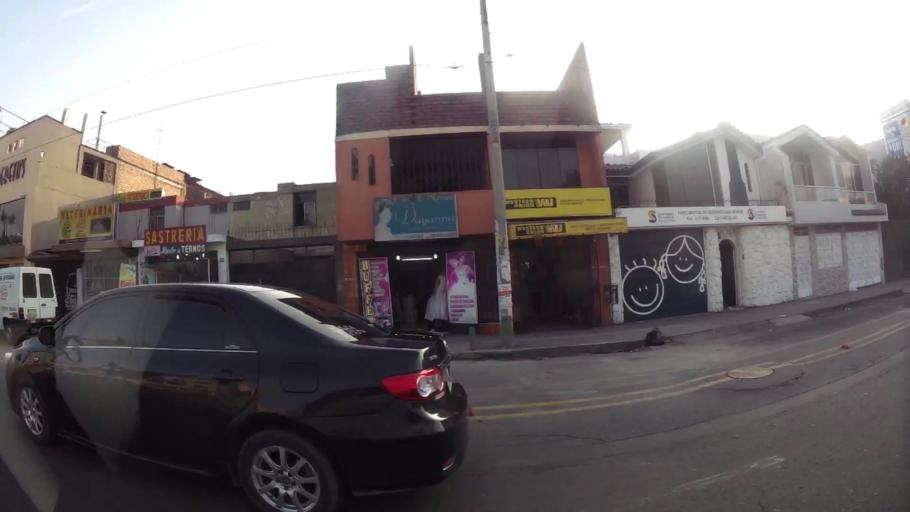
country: PE
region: Lima
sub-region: Lima
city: Independencia
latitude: -11.9877
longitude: -77.0726
